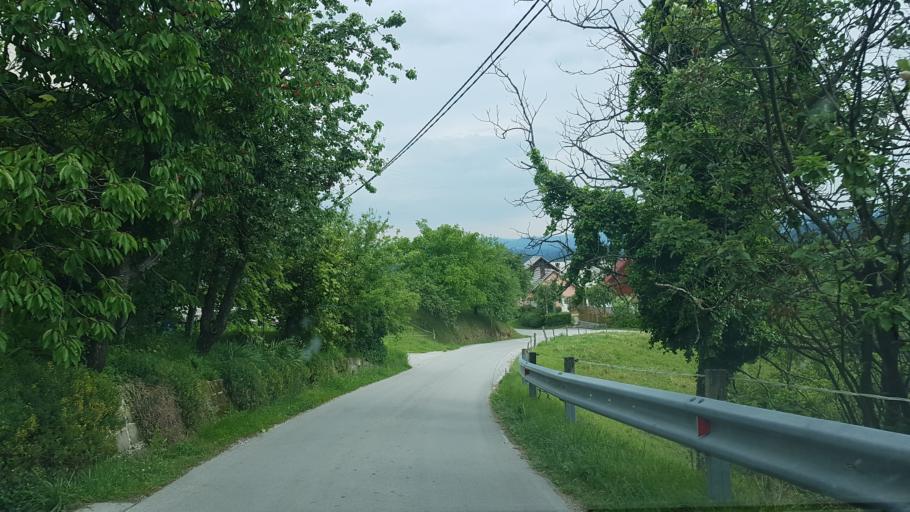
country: SI
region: Dobrna
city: Dobrna
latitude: 46.3473
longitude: 15.2401
